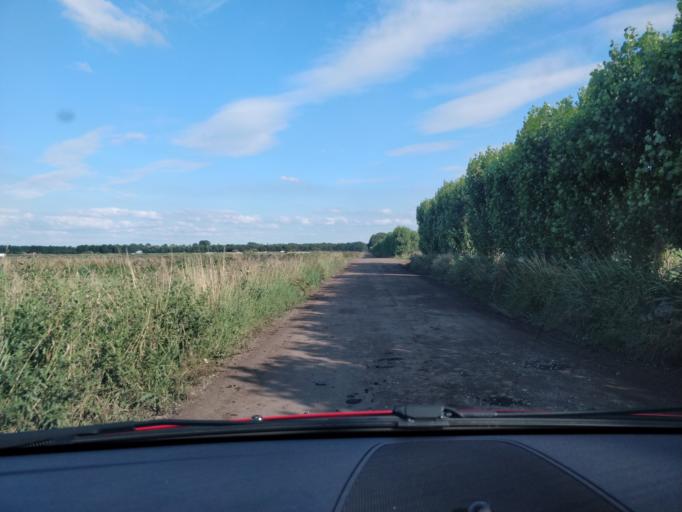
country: GB
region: England
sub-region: Lancashire
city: Banks
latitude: 53.6592
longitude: -2.9116
